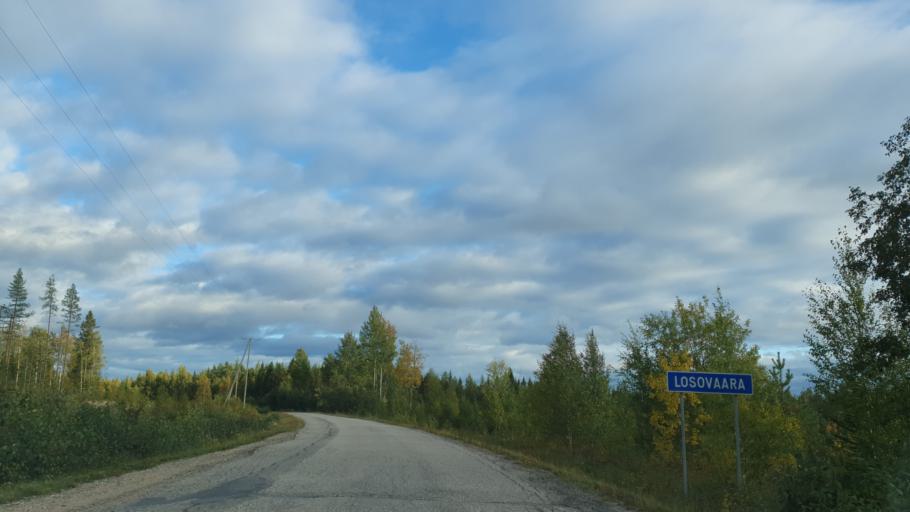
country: FI
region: Kainuu
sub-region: Kehys-Kainuu
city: Kuhmo
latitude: 63.9163
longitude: 30.0717
